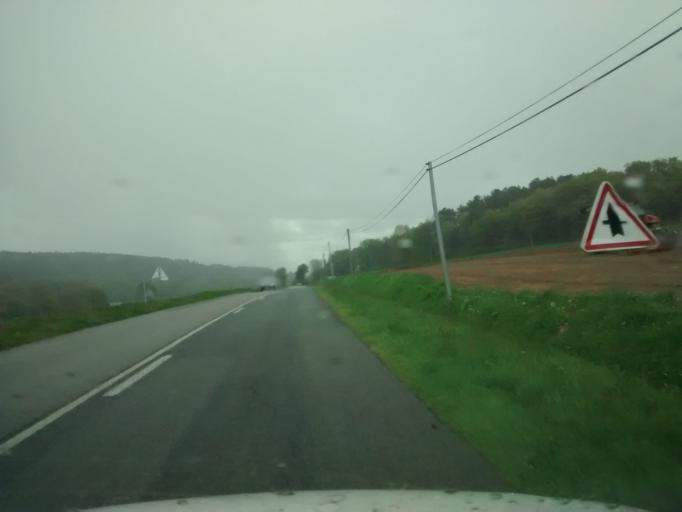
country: FR
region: Brittany
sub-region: Departement du Morbihan
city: Ruffiac
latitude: 47.7846
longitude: -2.3185
